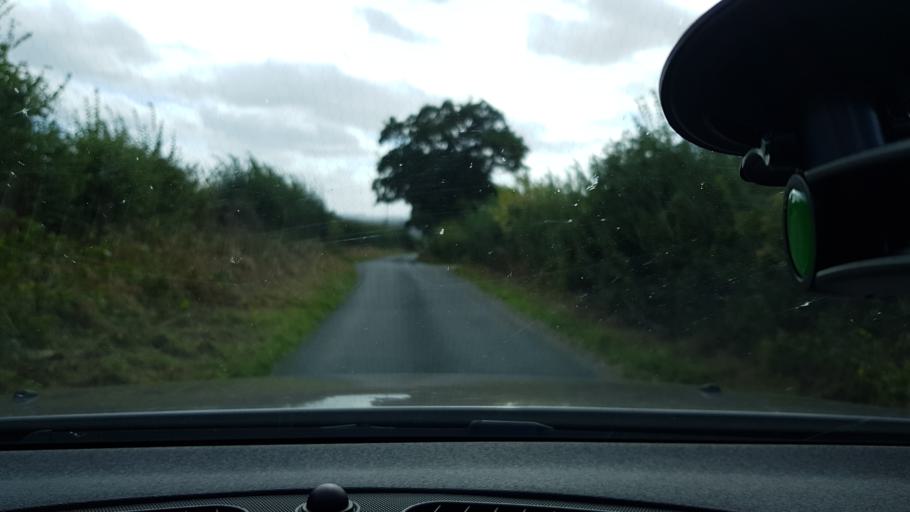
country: GB
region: England
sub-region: West Berkshire
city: Hungerford
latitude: 51.4290
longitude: -1.5130
